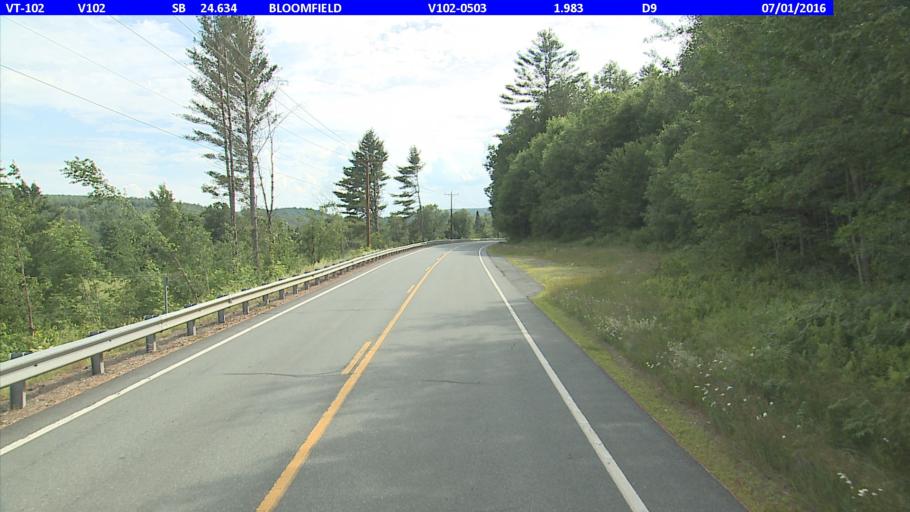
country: US
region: New Hampshire
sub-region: Coos County
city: Stratford
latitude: 44.7685
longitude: -71.6071
